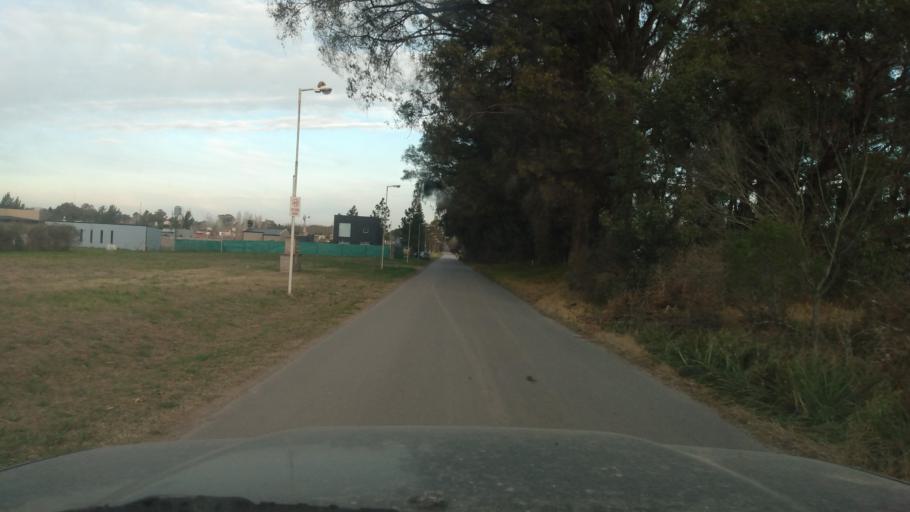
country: AR
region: Buenos Aires
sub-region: Partido de Lujan
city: Lujan
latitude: -34.5750
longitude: -59.0704
